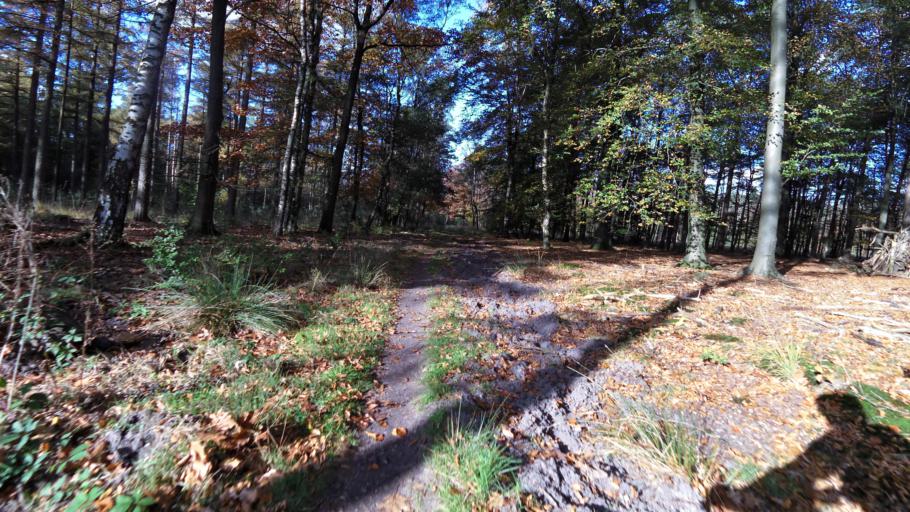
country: NL
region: Gelderland
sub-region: Gemeente Nunspeet
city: Nunspeet
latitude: 52.3531
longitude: 5.8191
